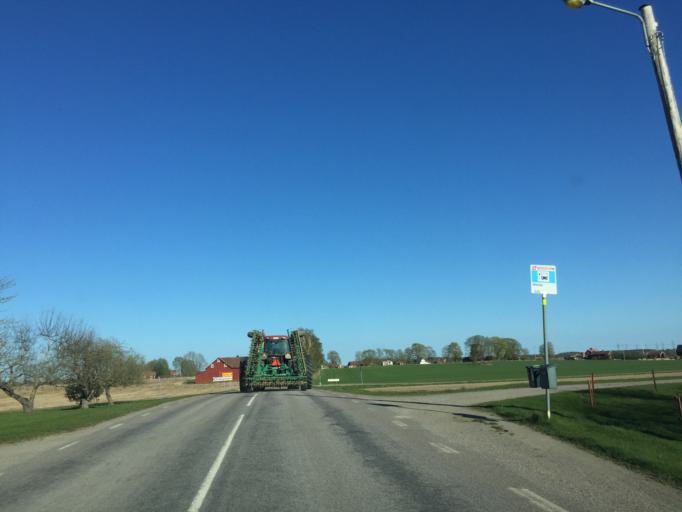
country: SE
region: OErebro
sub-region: Orebro Kommun
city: Odensbacken
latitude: 59.2048
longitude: 15.5413
